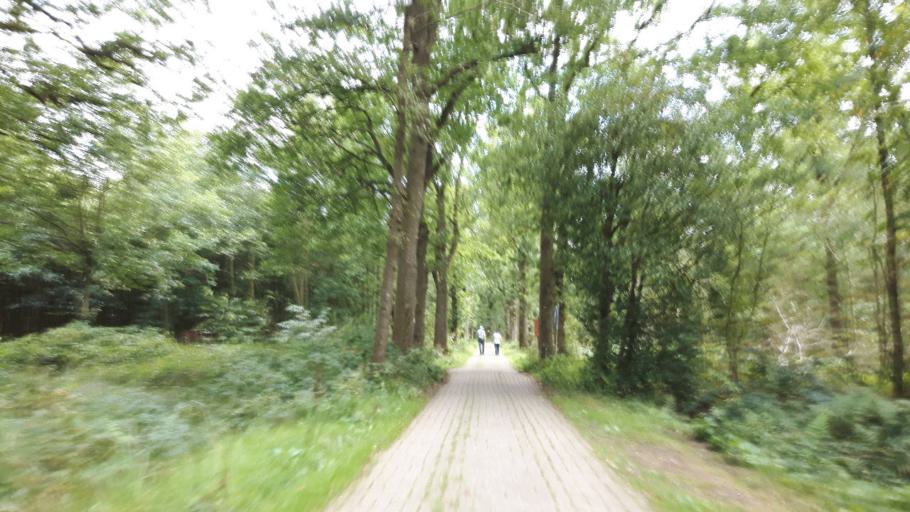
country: NL
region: Friesland
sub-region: Gemeente Smallingerland
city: Drachtstercompagnie
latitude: 53.0633
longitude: 6.2212
